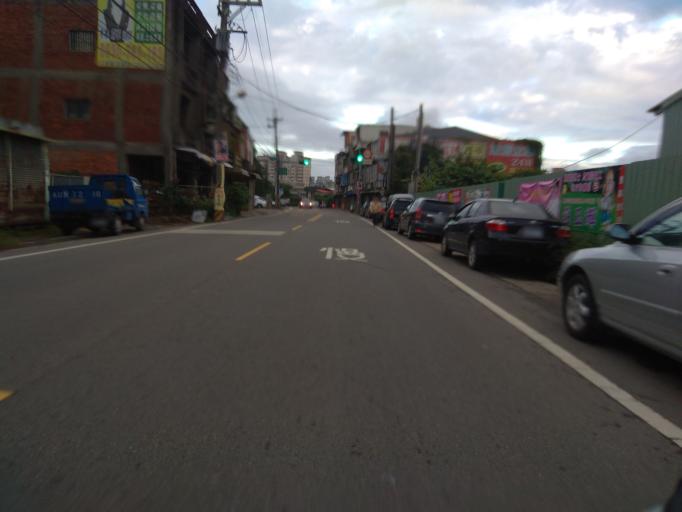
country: TW
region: Taiwan
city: Daxi
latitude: 24.9441
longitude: 121.1973
